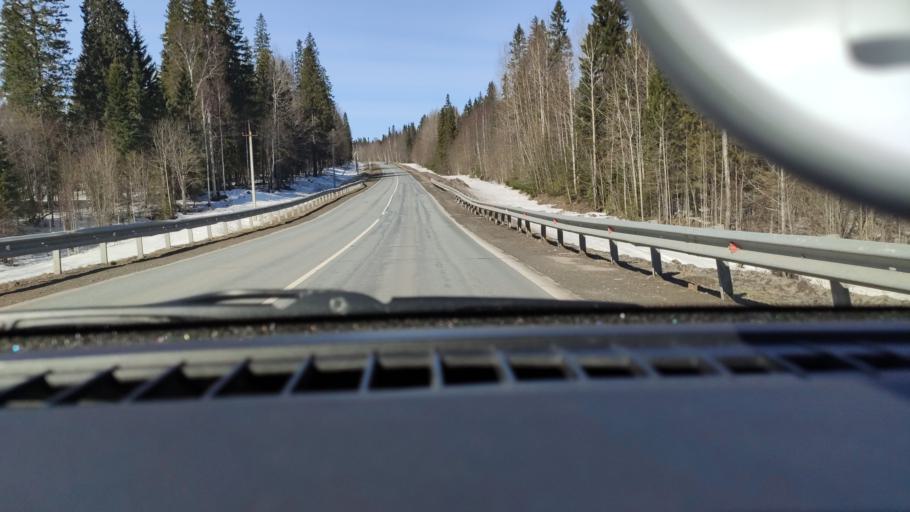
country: RU
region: Perm
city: Perm
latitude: 58.2026
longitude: 56.2030
